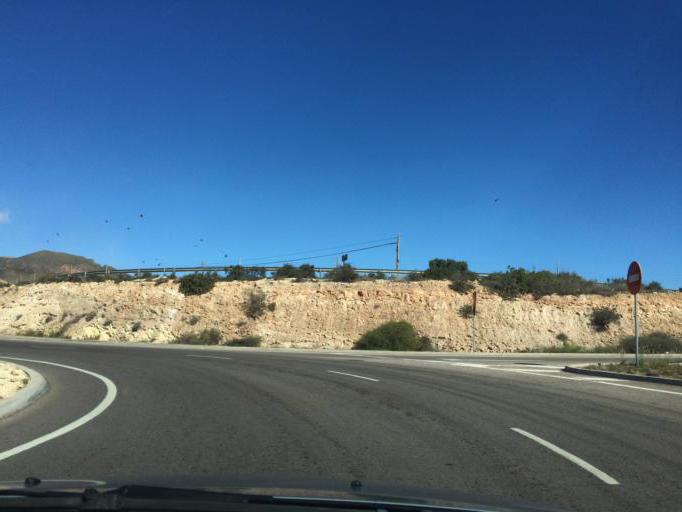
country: ES
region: Andalusia
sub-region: Provincia de Almeria
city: Nijar
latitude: 36.9381
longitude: -2.2072
